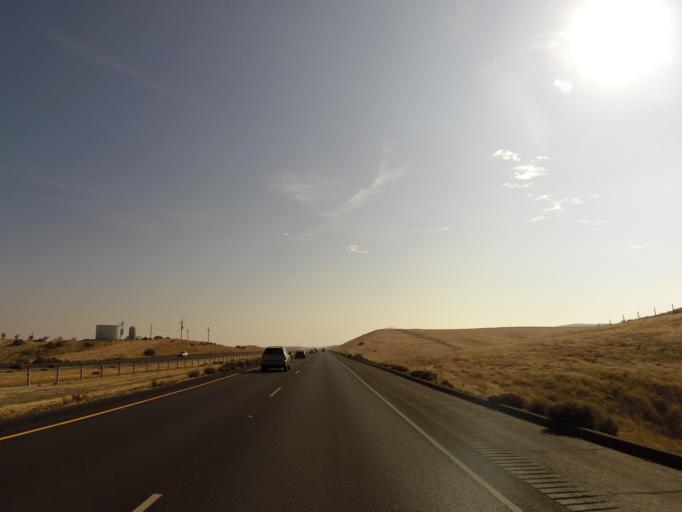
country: US
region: California
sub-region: Kings County
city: Avenal
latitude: 36.0444
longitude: -120.0483
